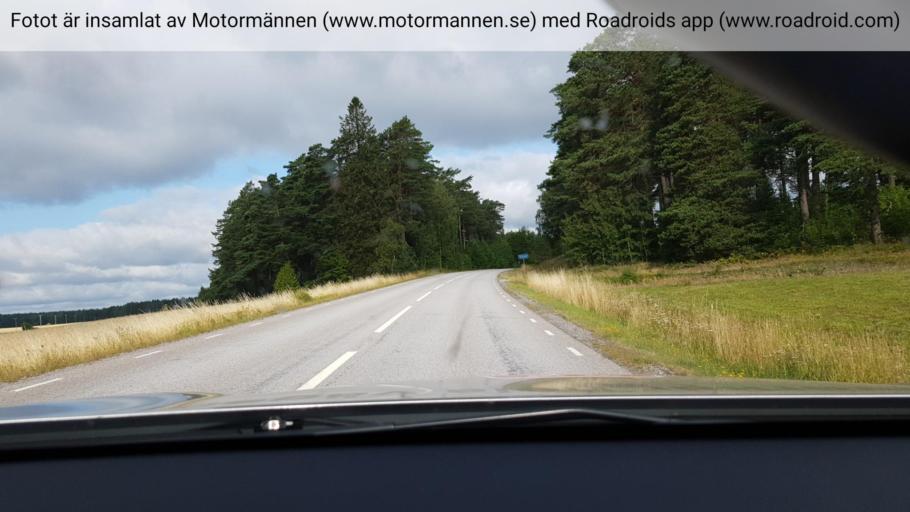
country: SE
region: Stockholm
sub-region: Norrtalje Kommun
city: Nykvarn
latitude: 59.8983
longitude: 18.3490
